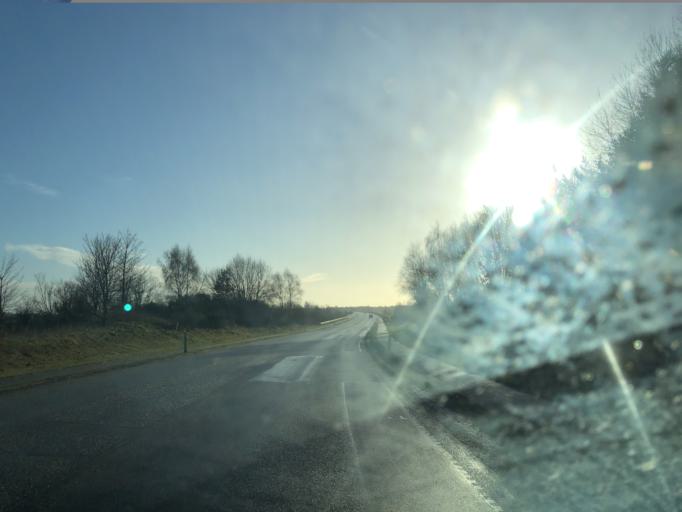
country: DK
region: Central Jutland
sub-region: Skive Kommune
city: Skive
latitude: 56.5490
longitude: 8.9918
